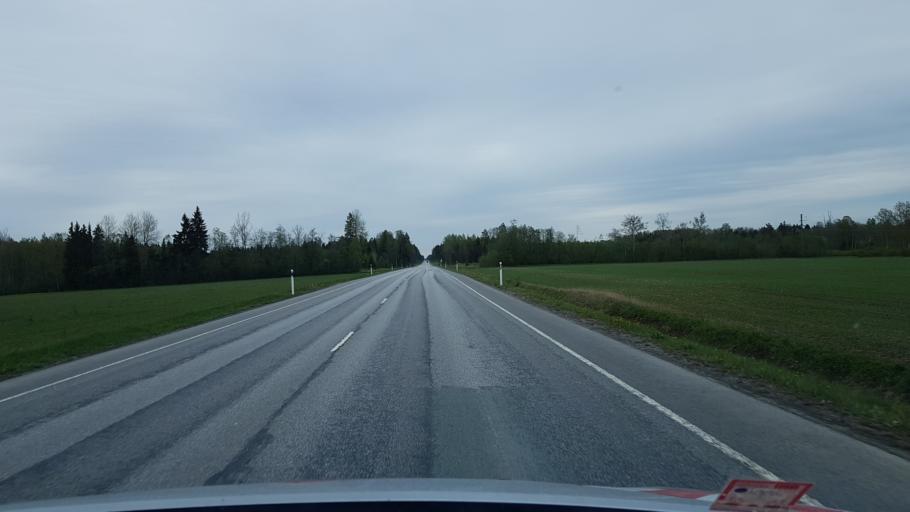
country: EE
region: Jaervamaa
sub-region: Paide linn
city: Paide
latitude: 58.9419
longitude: 25.6420
